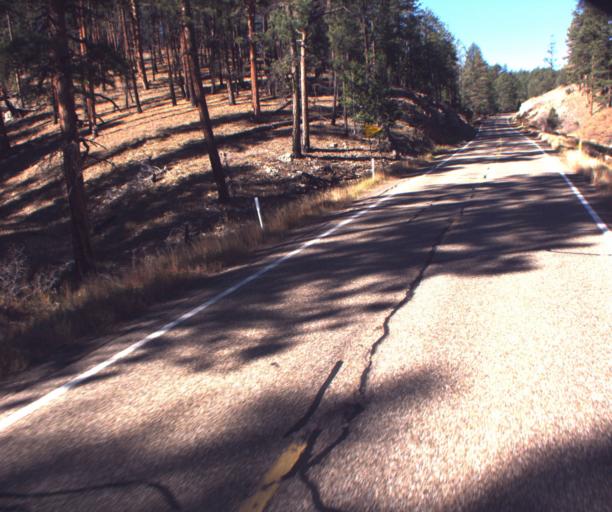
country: US
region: Arizona
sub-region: Coconino County
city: Fredonia
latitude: 36.7320
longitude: -112.1586
